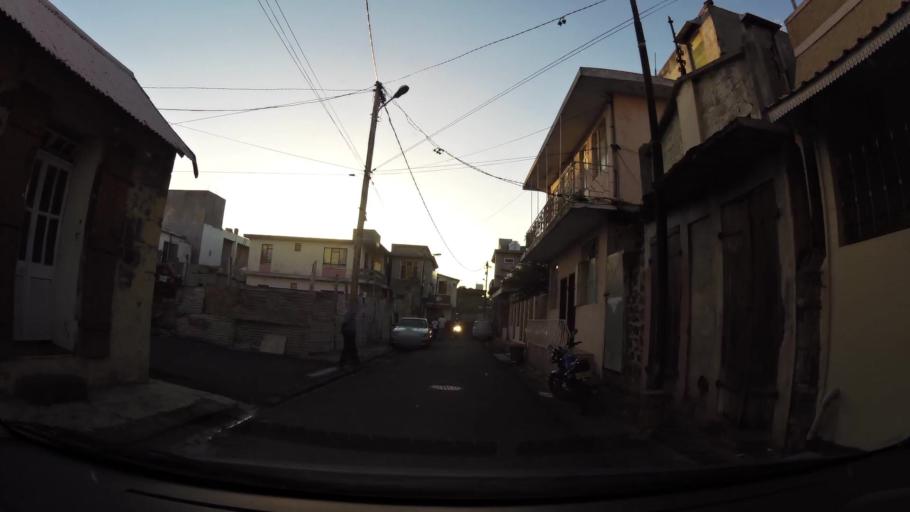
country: MU
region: Port Louis
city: Port Louis
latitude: -20.1546
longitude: 57.5102
